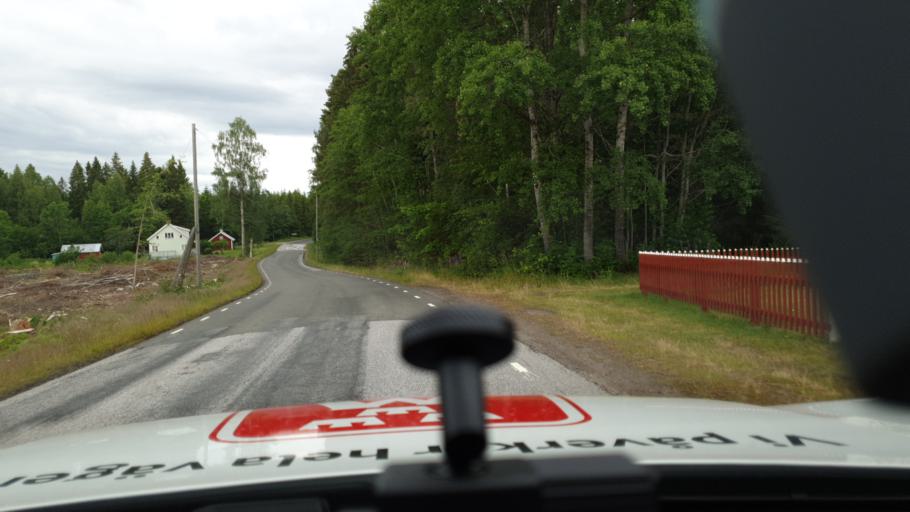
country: SE
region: Vaestra Goetaland
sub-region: Karlsborgs Kommun
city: Molltorp
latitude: 58.6734
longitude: 14.3602
